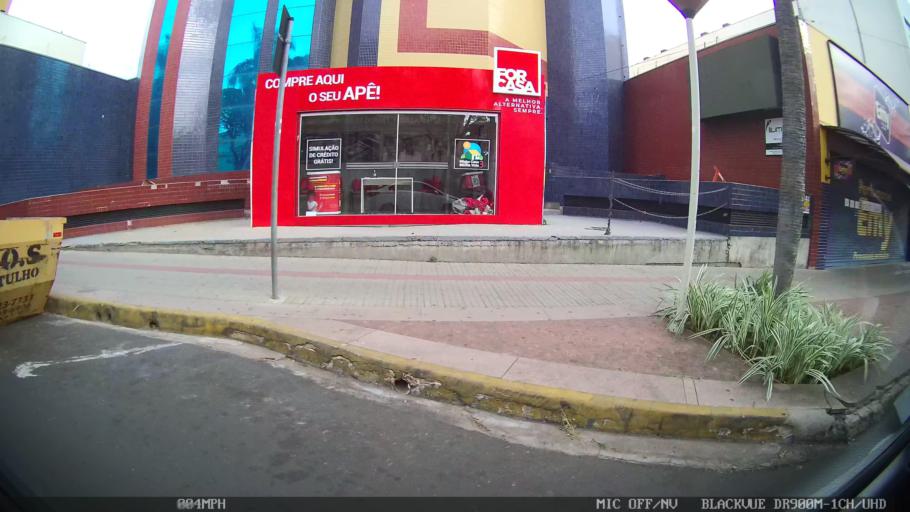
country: BR
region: Sao Paulo
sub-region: Catanduva
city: Catanduva
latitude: -21.1382
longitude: -48.9733
